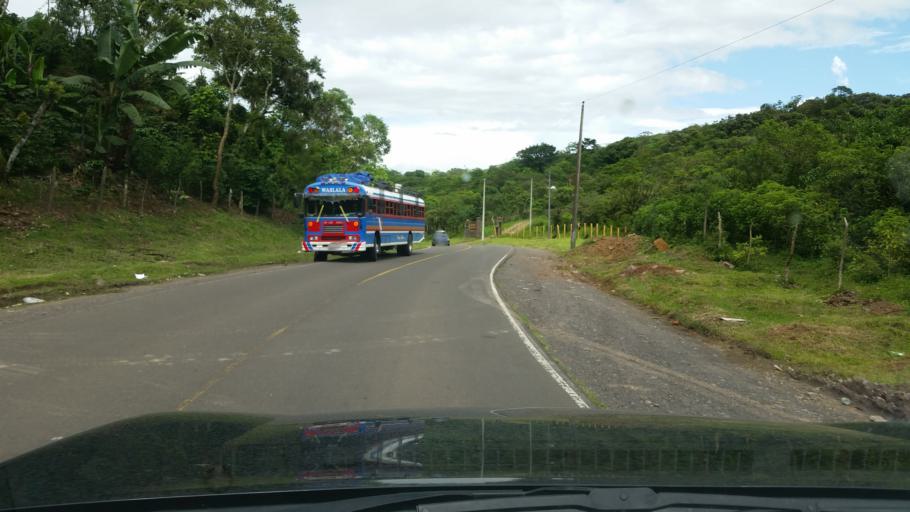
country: NI
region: Matagalpa
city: San Ramon
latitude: 12.9593
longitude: -85.8574
